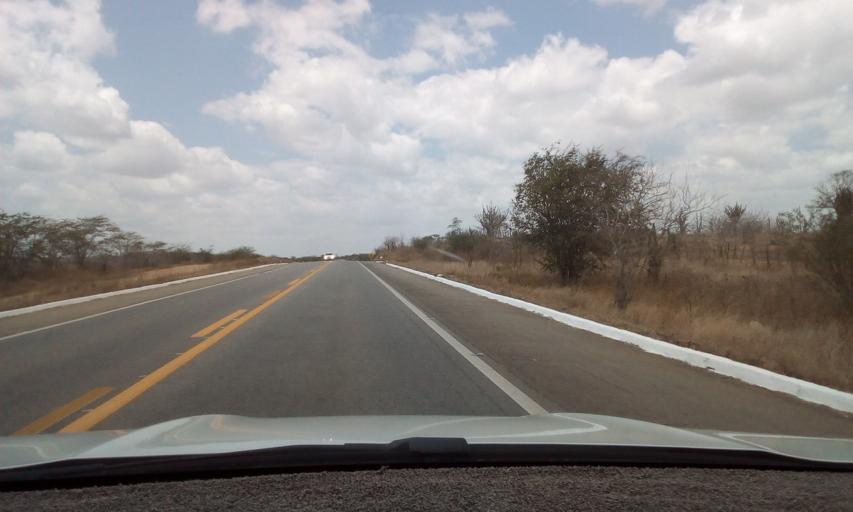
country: BR
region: Pernambuco
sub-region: Taquaritinga Do Norte
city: Taquaritinga do Norte
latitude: -7.7099
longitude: -36.0663
